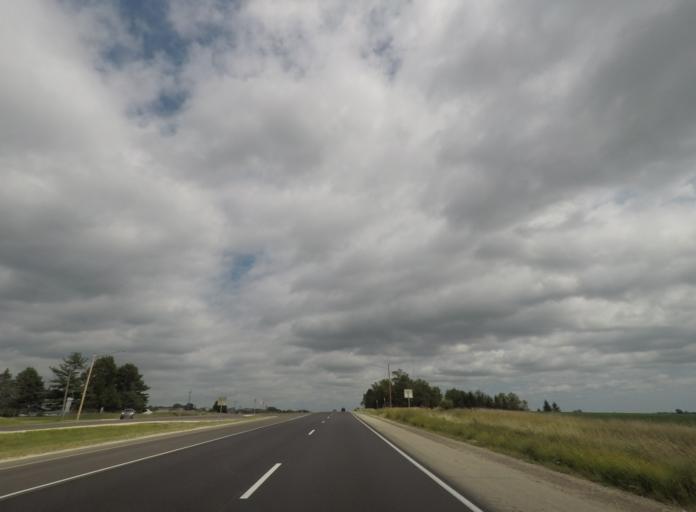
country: US
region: Iowa
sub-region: Linn County
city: Ely
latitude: 41.9263
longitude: -91.6256
